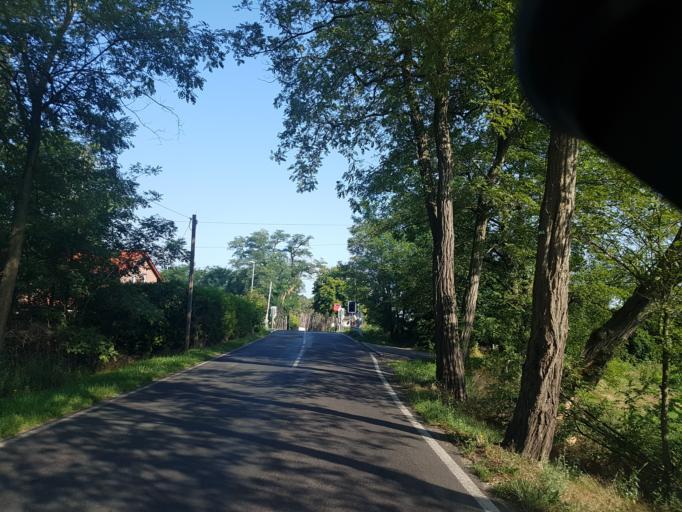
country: DE
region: Brandenburg
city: Niemegk
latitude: 52.1636
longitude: 12.6850
